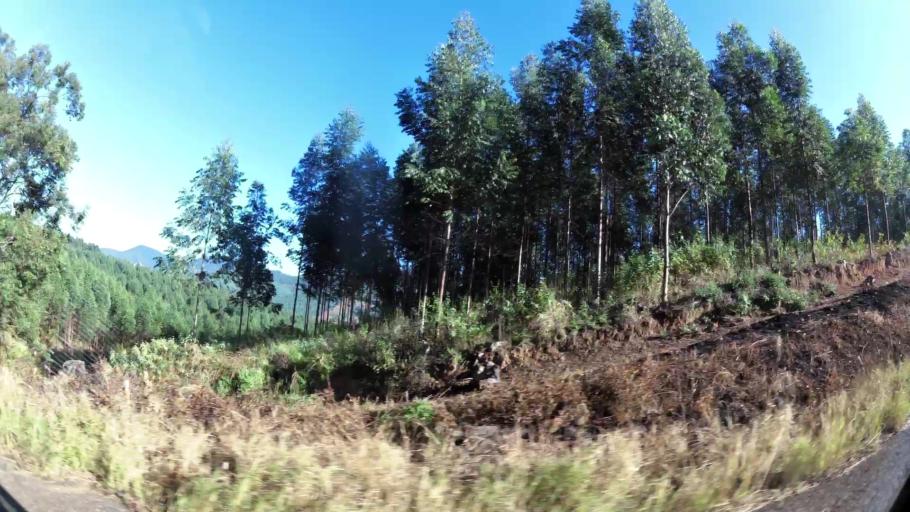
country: ZA
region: Limpopo
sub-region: Mopani District Municipality
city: Tzaneen
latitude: -23.8713
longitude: 30.1009
